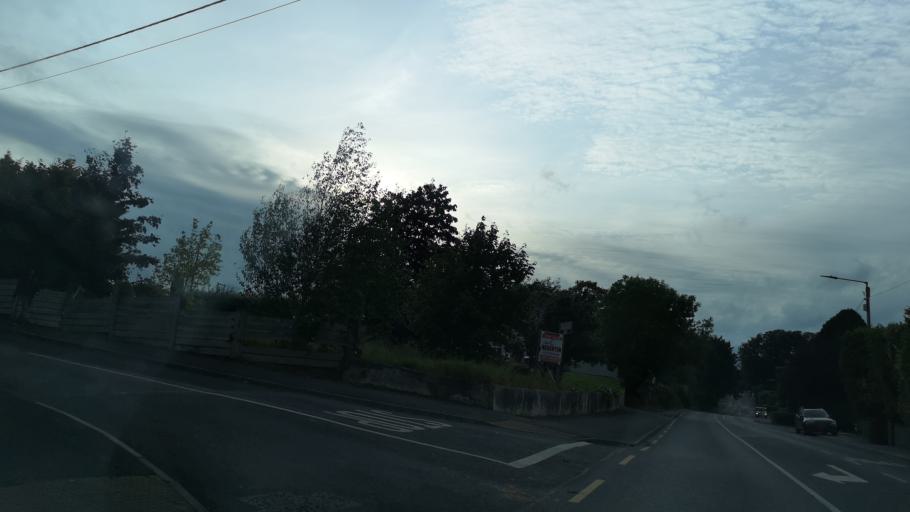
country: IE
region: Leinster
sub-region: An Iarmhi
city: Athlone
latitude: 53.4215
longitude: -7.9155
